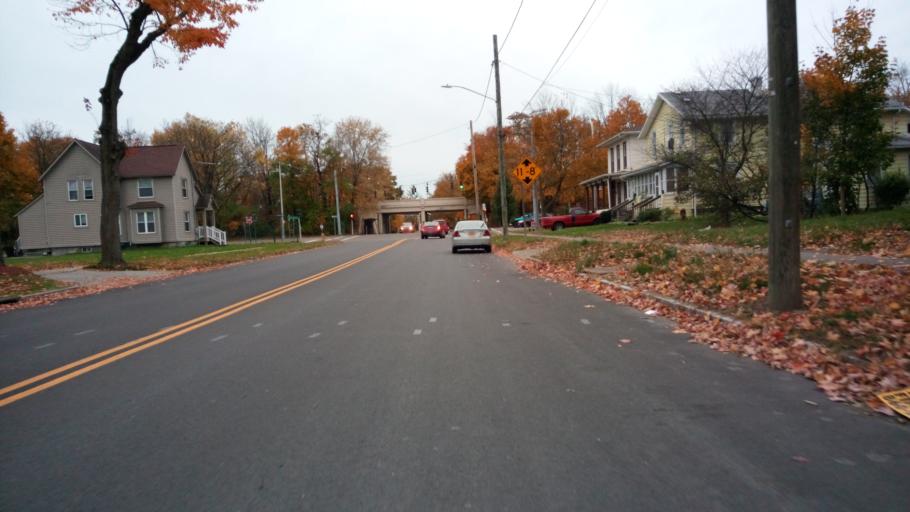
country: US
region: New York
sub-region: Chemung County
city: Elmira
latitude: 42.0843
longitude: -76.8014
